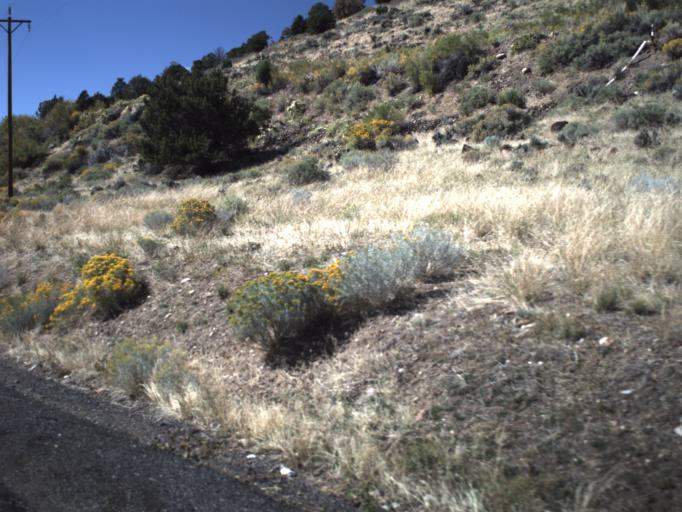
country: US
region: Utah
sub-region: Beaver County
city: Beaver
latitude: 38.2822
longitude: -112.5881
